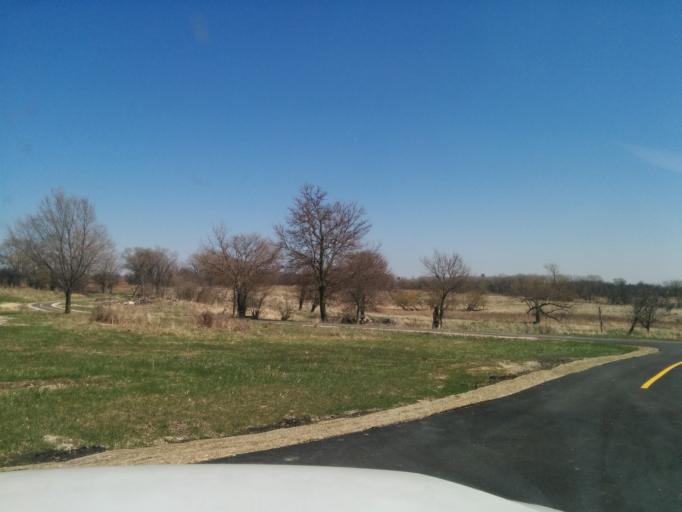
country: US
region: Illinois
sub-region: Cook County
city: Oak Forest
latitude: 41.6010
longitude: -87.7293
